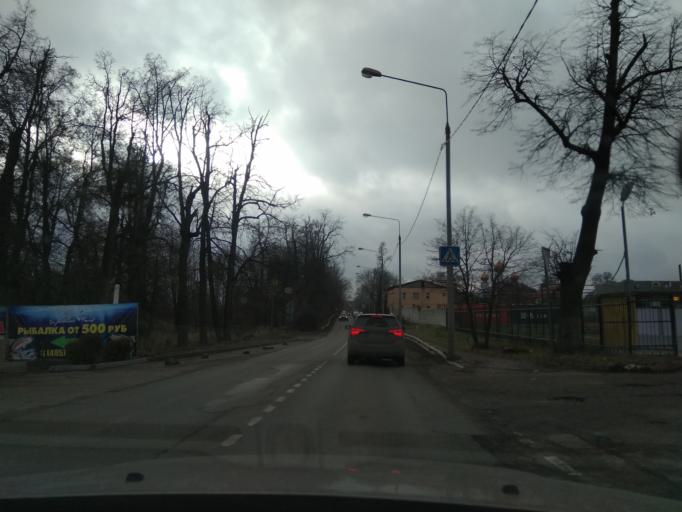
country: RU
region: Moscow
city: Zagor'ye
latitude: 55.5631
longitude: 37.6861
